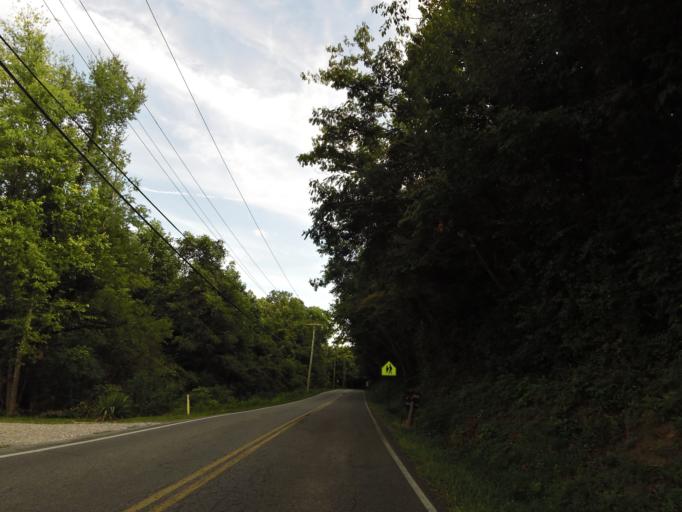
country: US
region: Tennessee
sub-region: Blount County
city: Wildwood
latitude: 35.8425
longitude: -83.8029
